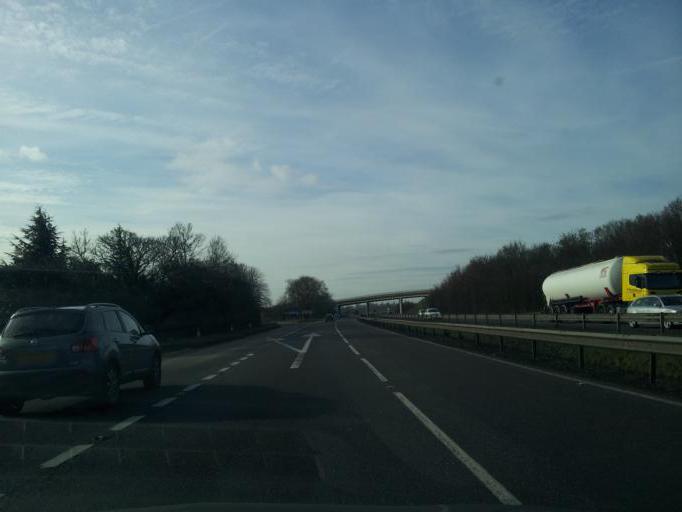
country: GB
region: England
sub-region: Cambridgeshire
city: Little Paxton
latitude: 52.2544
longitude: -0.2646
